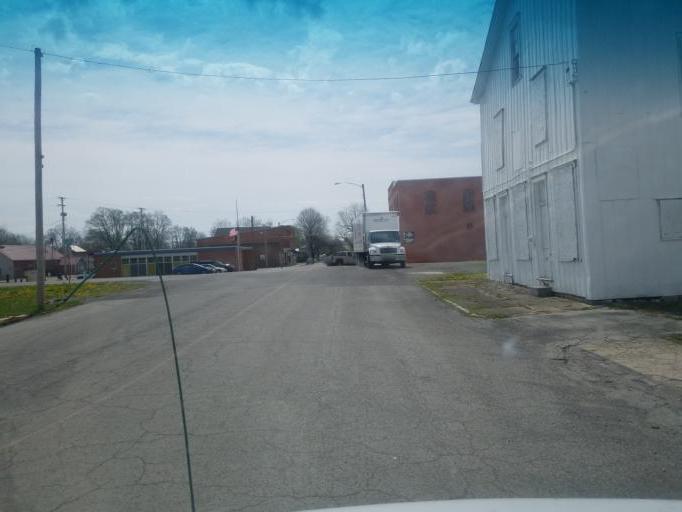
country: US
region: Ohio
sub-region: Logan County
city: Northwood
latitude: 40.5083
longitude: -83.7532
